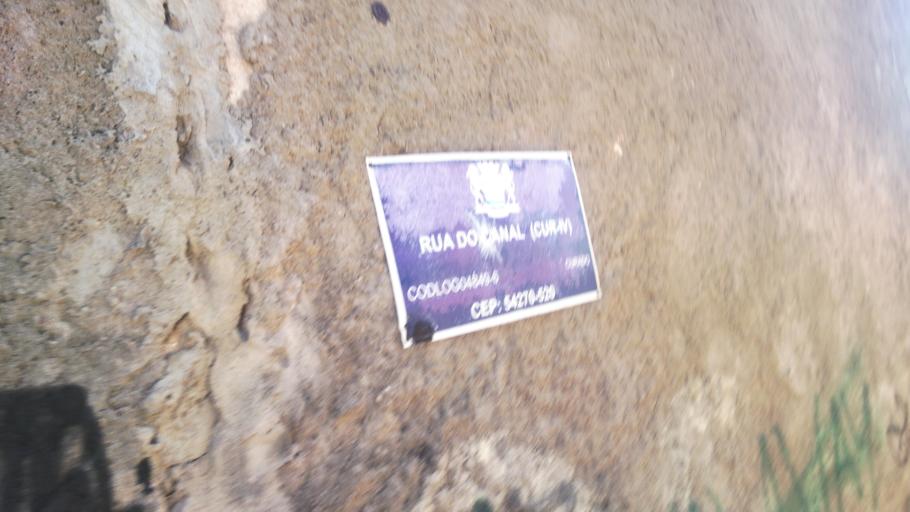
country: BR
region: Pernambuco
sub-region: Jaboatao Dos Guararapes
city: Jaboatao dos Guararapes
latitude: -8.0696
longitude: -34.9981
